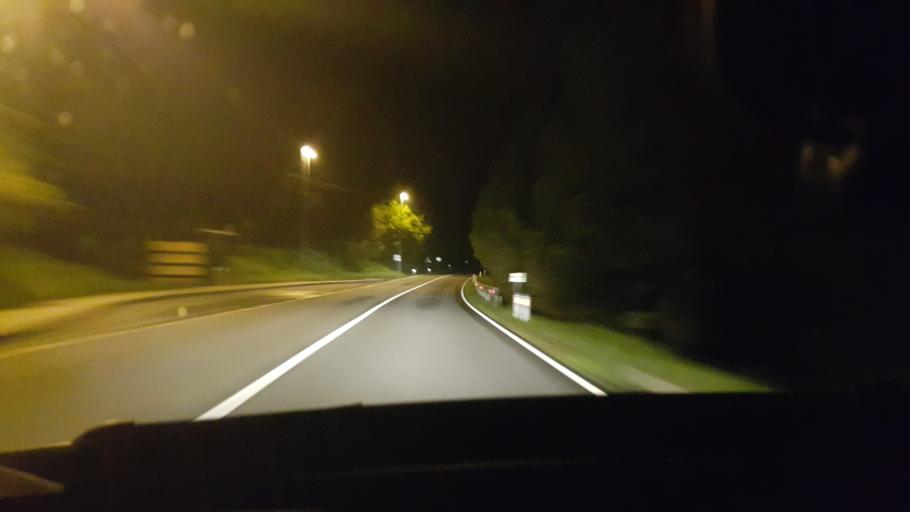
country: SI
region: Podvelka
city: Podvelka
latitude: 46.5840
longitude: 15.3676
